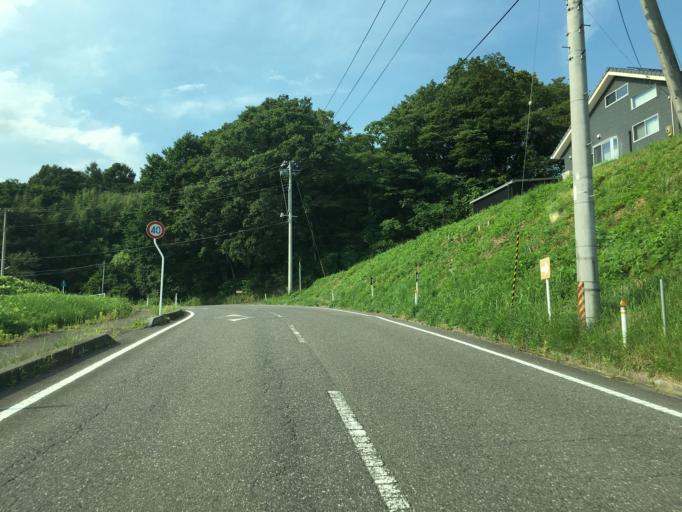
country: JP
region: Fukushima
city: Miharu
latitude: 37.4282
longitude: 140.4530
